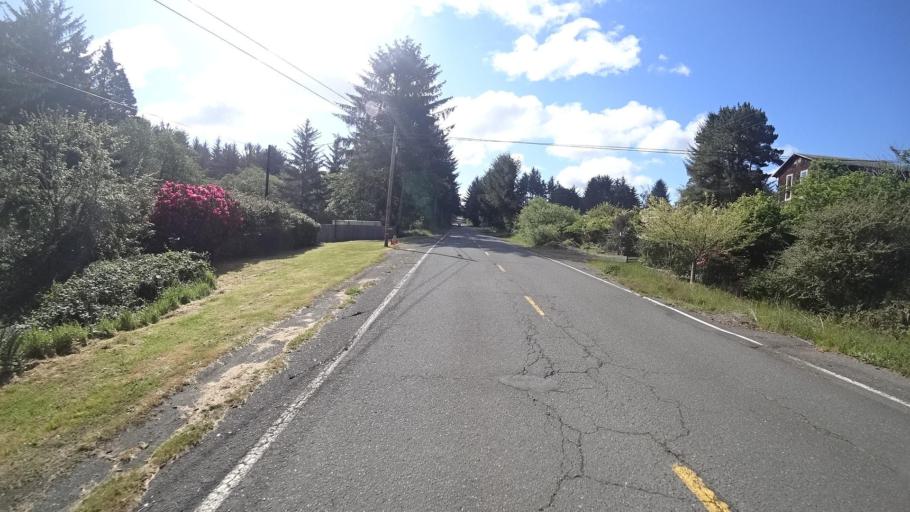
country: US
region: California
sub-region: Humboldt County
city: McKinleyville
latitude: 40.9878
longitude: -124.1088
